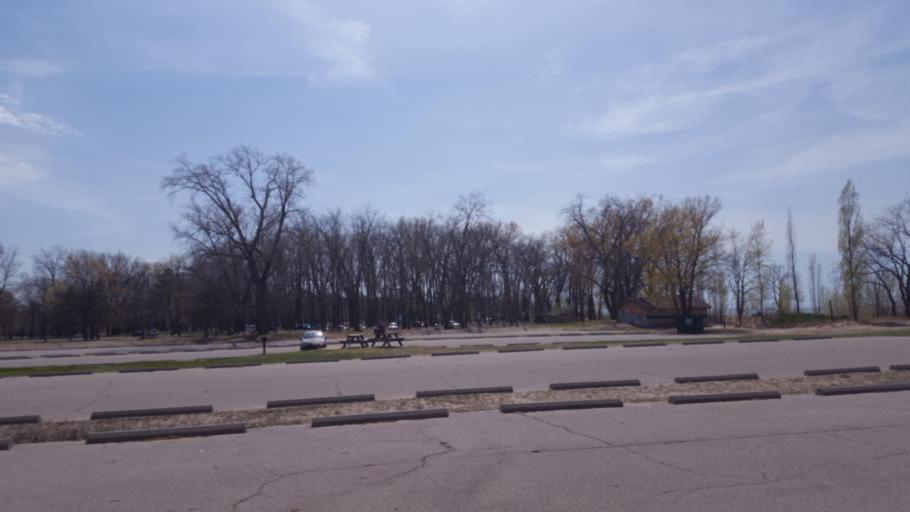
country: US
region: Ohio
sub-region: Lake County
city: Fairport Harbor
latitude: 41.7573
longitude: -81.2874
